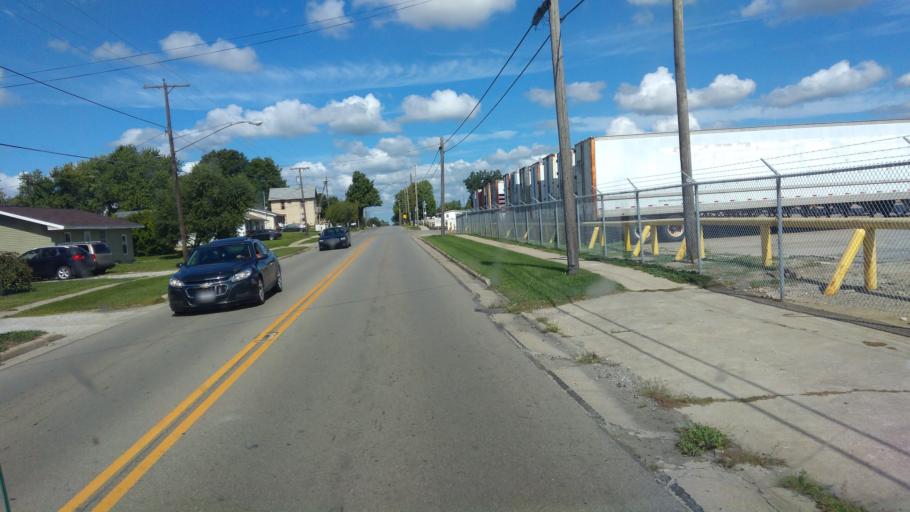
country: US
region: Ohio
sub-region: Huron County
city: Willard
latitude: 41.0466
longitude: -82.7158
